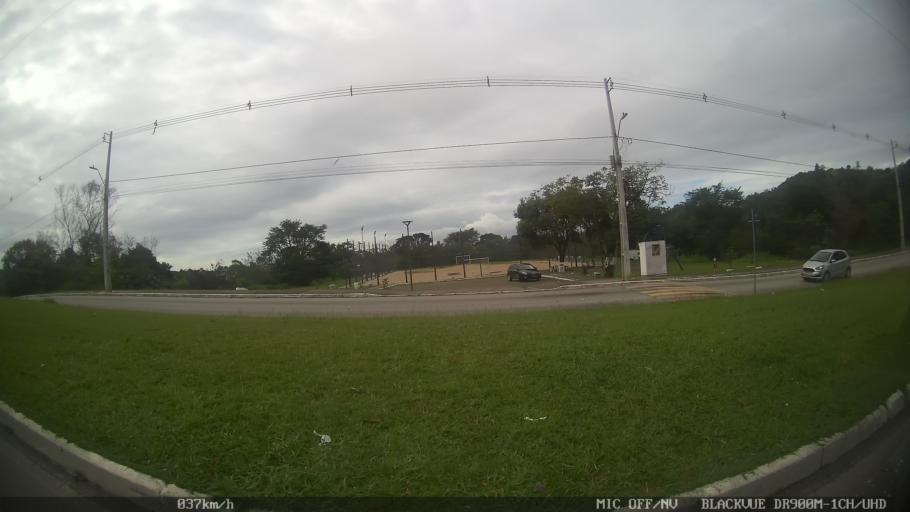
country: BR
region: Santa Catarina
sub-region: Biguacu
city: Biguacu
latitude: -27.5453
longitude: -48.6479
